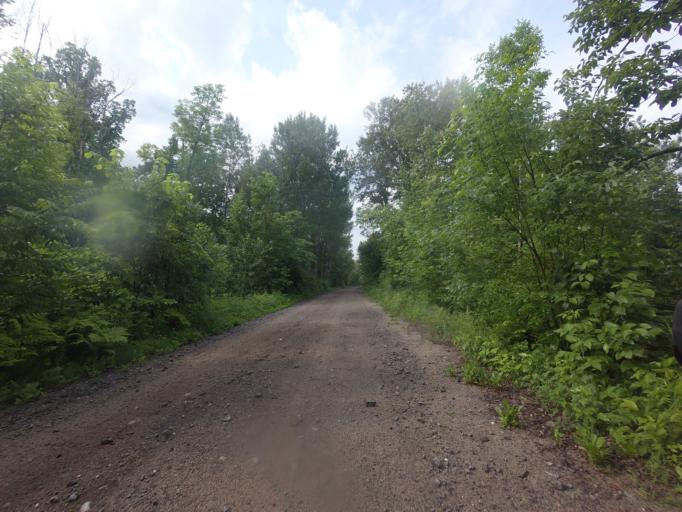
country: CA
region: Quebec
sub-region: Outaouais
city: Maniwaki
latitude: 46.3249
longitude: -76.0049
